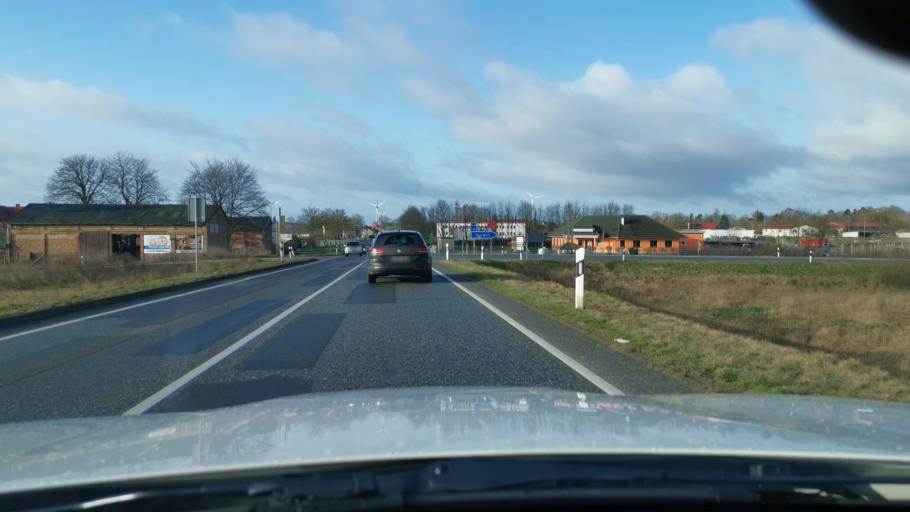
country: DE
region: Mecklenburg-Vorpommern
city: Laage
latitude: 53.8883
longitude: 12.2572
